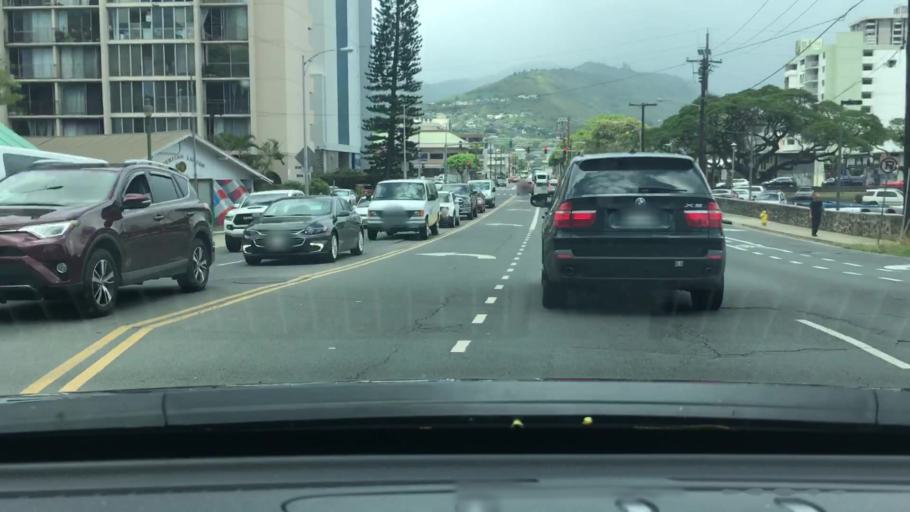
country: US
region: Hawaii
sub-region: Honolulu County
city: Honolulu
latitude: 21.2884
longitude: -157.8328
